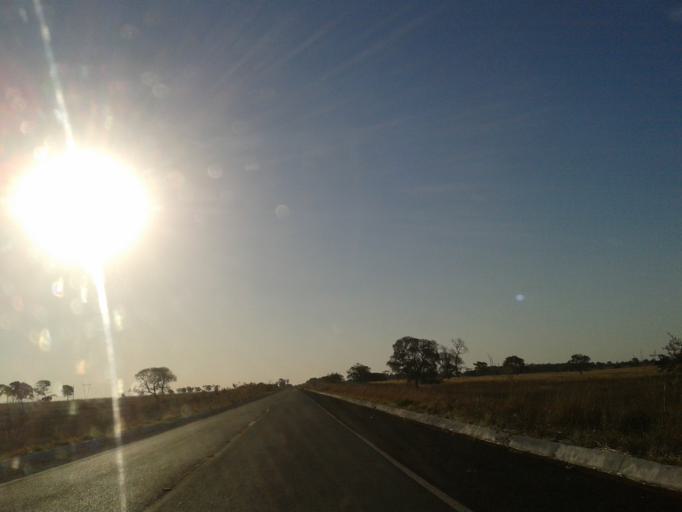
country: BR
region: Minas Gerais
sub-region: Santa Vitoria
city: Santa Vitoria
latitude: -19.1017
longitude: -50.3302
